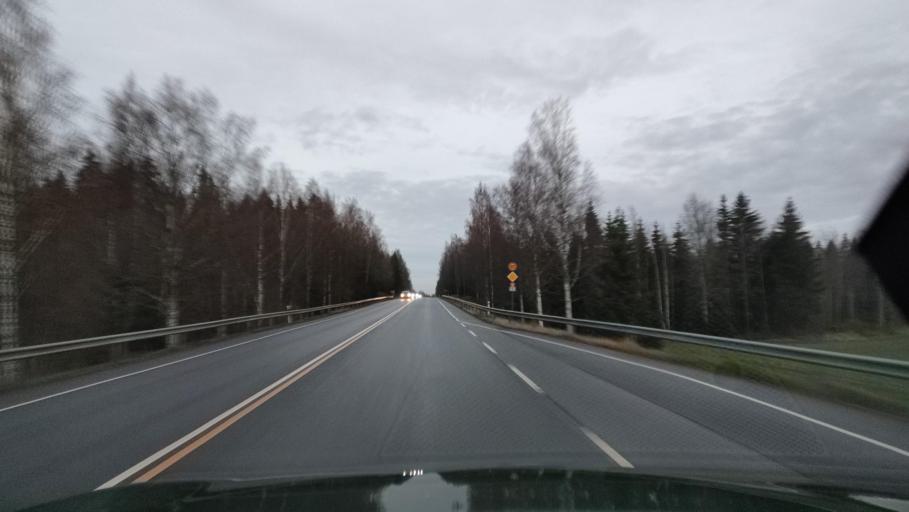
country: FI
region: Ostrobothnia
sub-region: Vaasa
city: Ristinummi
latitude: 62.9864
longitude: 21.7676
